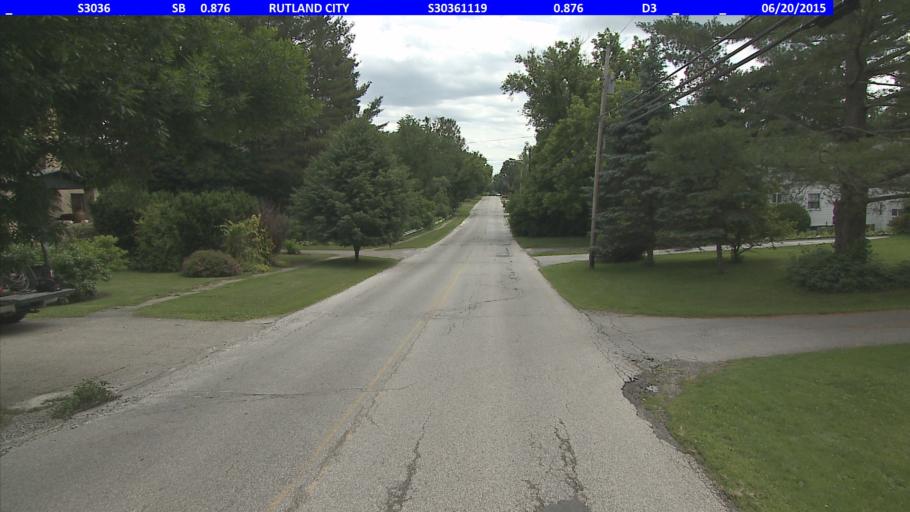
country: US
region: Vermont
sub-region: Rutland County
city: Rutland
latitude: 43.6209
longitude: -72.9780
